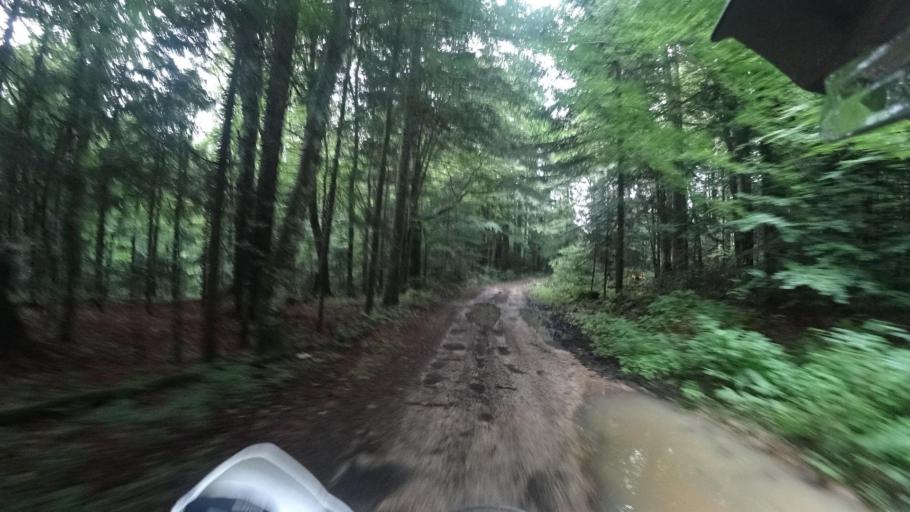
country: HR
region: Licko-Senjska
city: Jezerce
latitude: 44.7997
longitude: 15.6454
